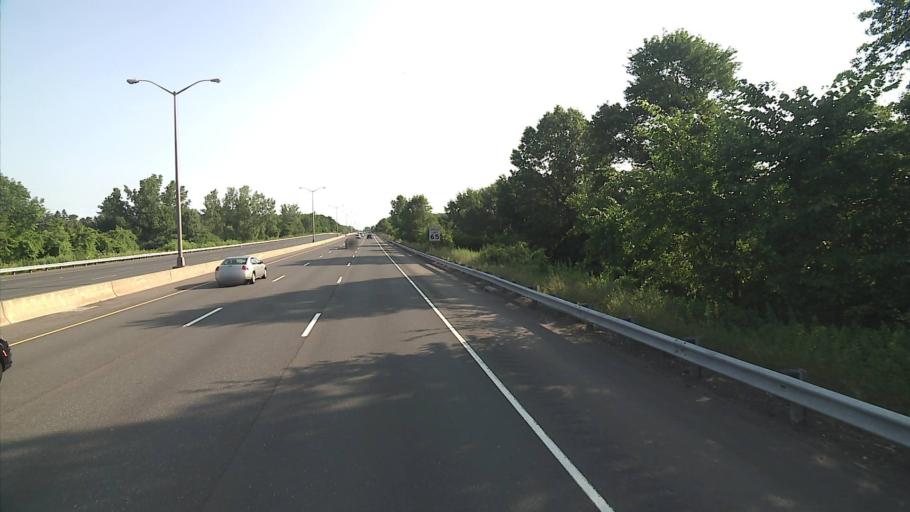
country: US
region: Connecticut
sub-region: Hartford County
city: Enfield
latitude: 41.9603
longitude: -72.5915
